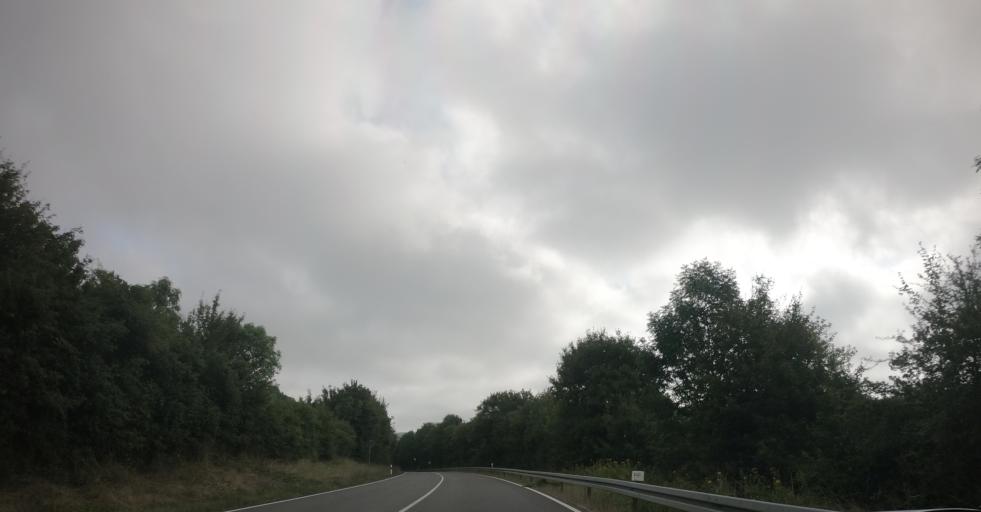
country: FR
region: Lorraine
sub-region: Departement de la Moselle
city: Bliesbruck
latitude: 49.1369
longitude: 7.1398
